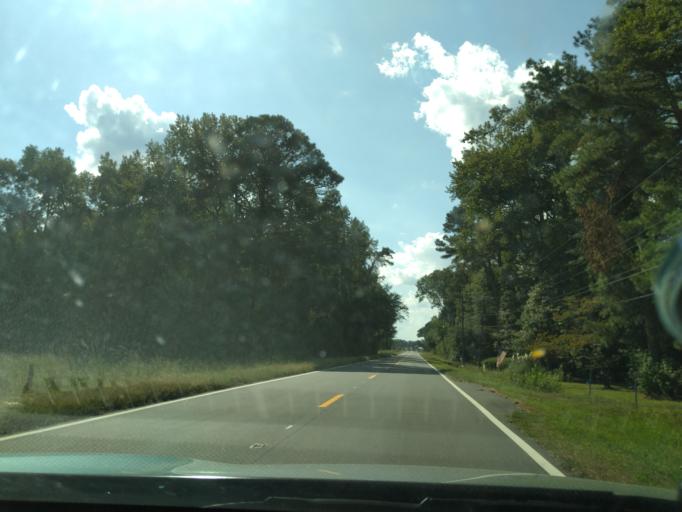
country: US
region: North Carolina
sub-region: Pitt County
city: Bethel
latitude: 35.8053
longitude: -77.3865
